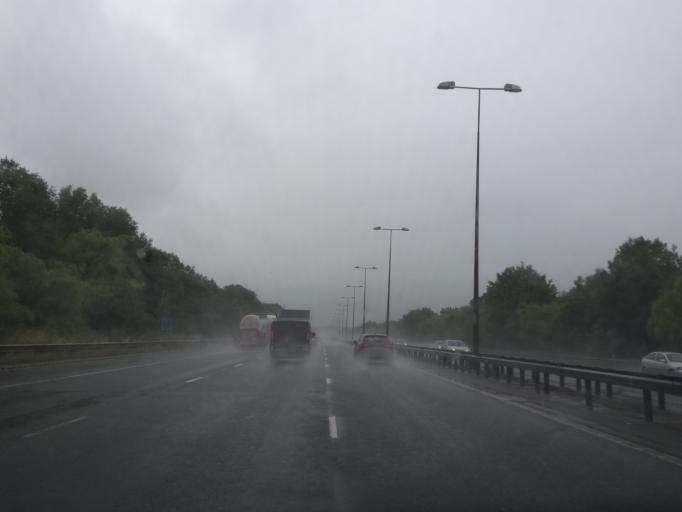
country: GB
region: England
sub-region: Leicestershire
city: Castle Donington
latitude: 52.8700
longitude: -1.3073
